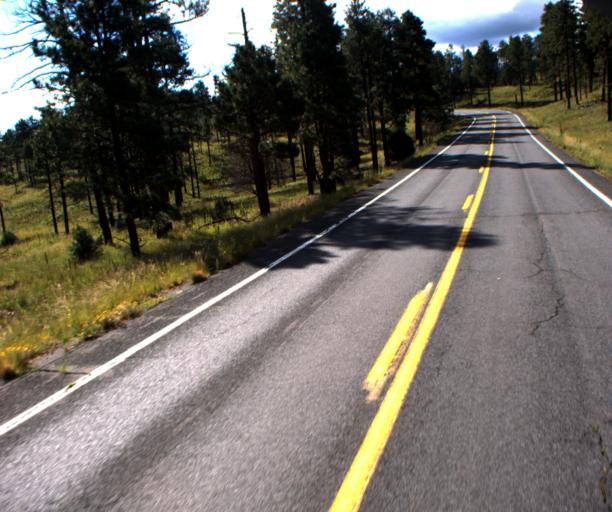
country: US
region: Arizona
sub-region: Apache County
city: Eagar
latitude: 34.0631
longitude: -109.3556
